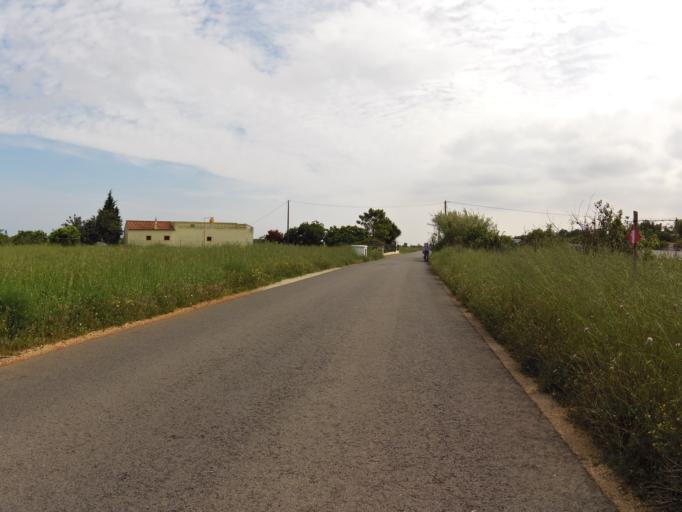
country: PT
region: Faro
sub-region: Silves
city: Armacao de Pera
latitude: 37.1139
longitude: -8.3473
